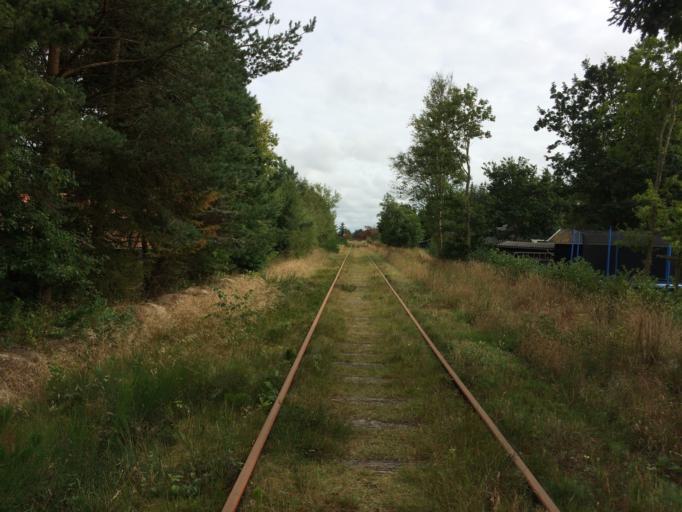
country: DK
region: South Denmark
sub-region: Varde Kommune
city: Oksbol
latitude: 55.7950
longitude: 8.2270
